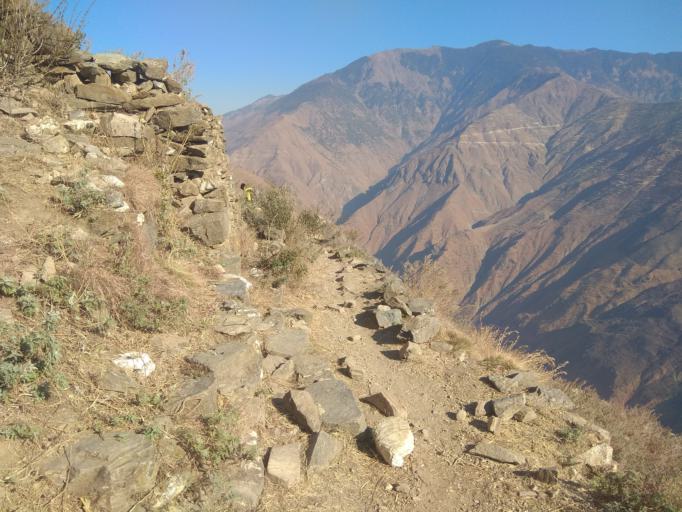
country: NP
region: Mid Western
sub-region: Karnali Zone
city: Jumla
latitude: 29.3131
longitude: 81.7423
